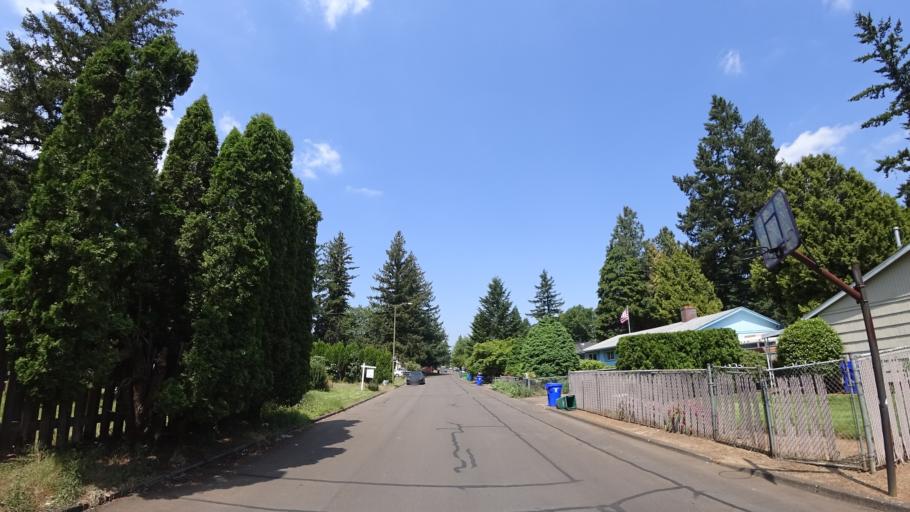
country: US
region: Oregon
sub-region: Multnomah County
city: Fairview
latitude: 45.5233
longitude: -122.4909
